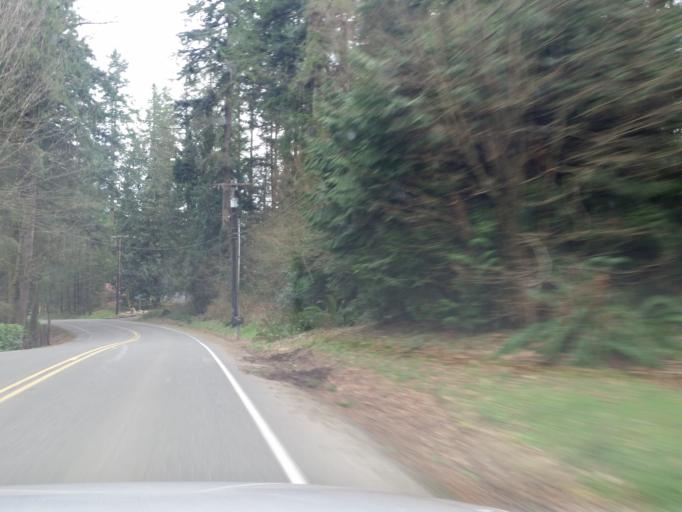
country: US
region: Washington
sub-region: King County
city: Cottage Lake
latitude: 47.7483
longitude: -122.1076
